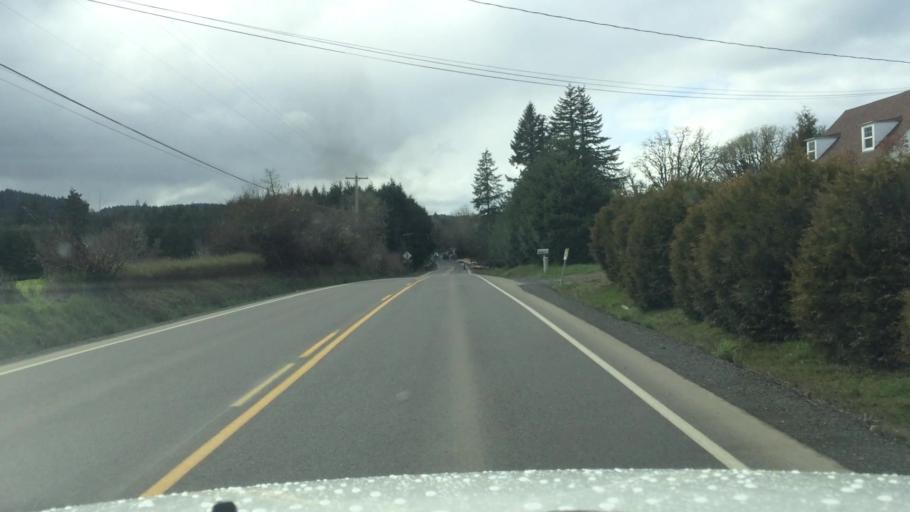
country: US
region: Oregon
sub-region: Polk County
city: Grand Ronde
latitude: 45.0800
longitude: -123.6132
